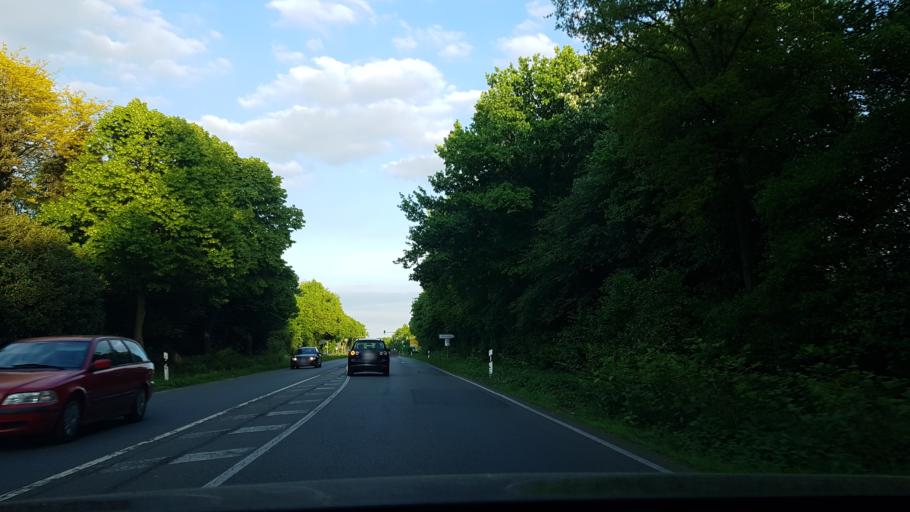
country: DE
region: North Rhine-Westphalia
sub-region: Regierungsbezirk Dusseldorf
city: Moers
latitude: 51.4408
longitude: 6.6185
